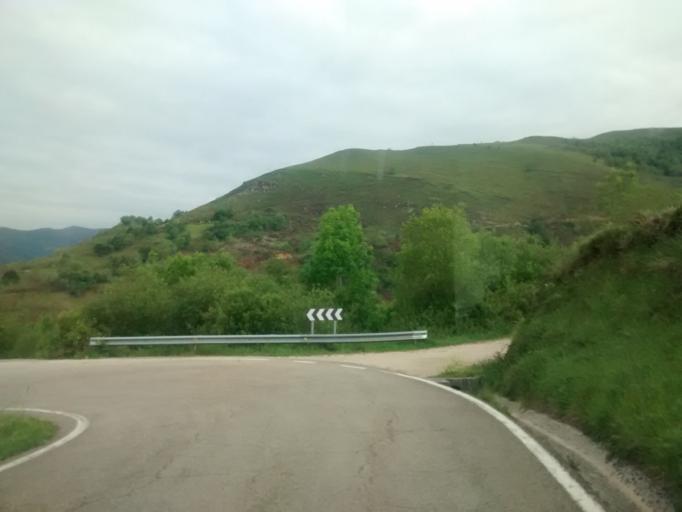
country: ES
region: Cantabria
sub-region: Provincia de Cantabria
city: San Vicente de la Barquera
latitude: 43.2505
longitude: -4.4268
